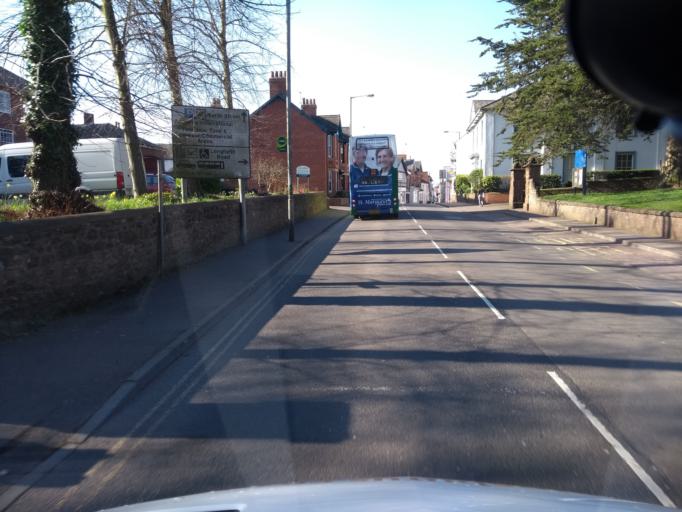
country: GB
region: England
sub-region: Somerset
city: Bishops Lydeard
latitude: 50.9808
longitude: -3.2244
